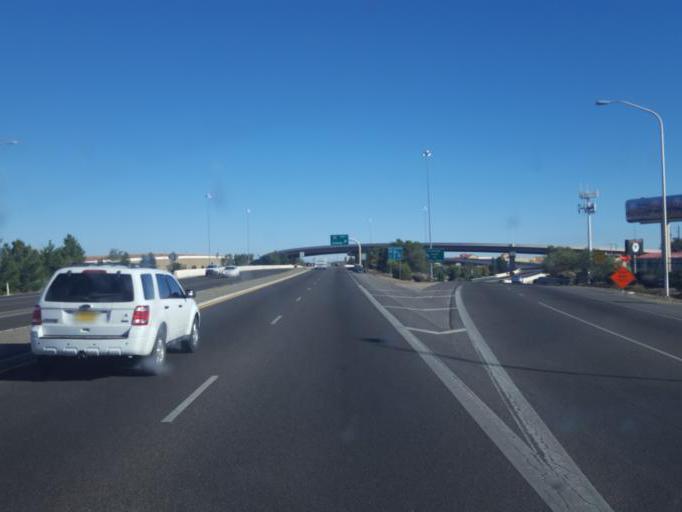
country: US
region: New Mexico
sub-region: Bernalillo County
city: Albuquerque
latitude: 35.1040
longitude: -106.7055
